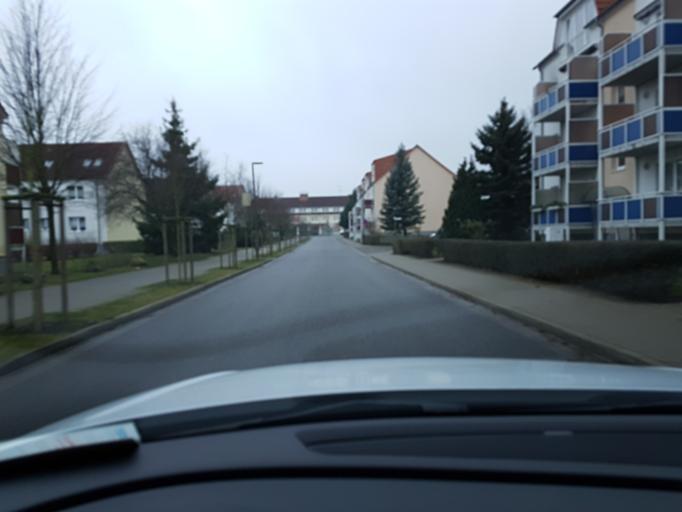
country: DE
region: Mecklenburg-Vorpommern
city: Ostseebad Binz
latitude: 54.4060
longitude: 13.6034
